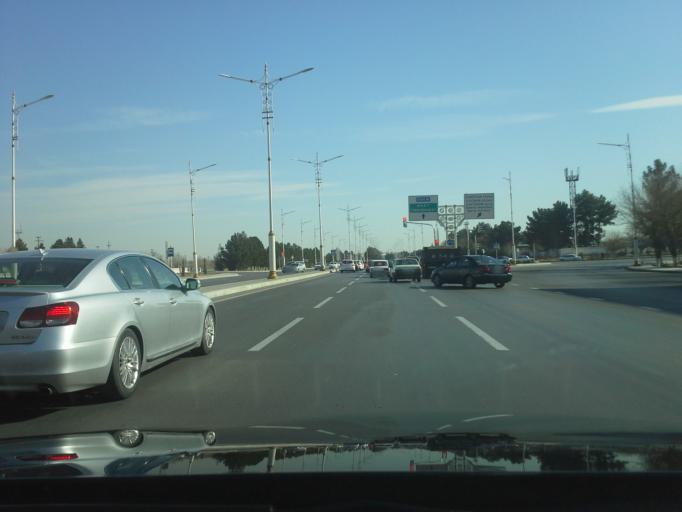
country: TM
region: Ahal
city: Ashgabat
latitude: 37.9233
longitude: 58.4391
